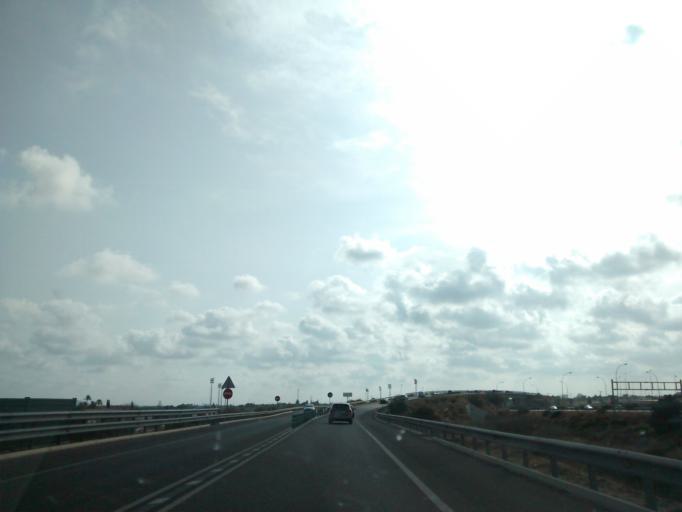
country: ES
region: Valencia
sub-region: Provincia de Alicante
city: el Campello
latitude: 38.4389
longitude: -0.4002
